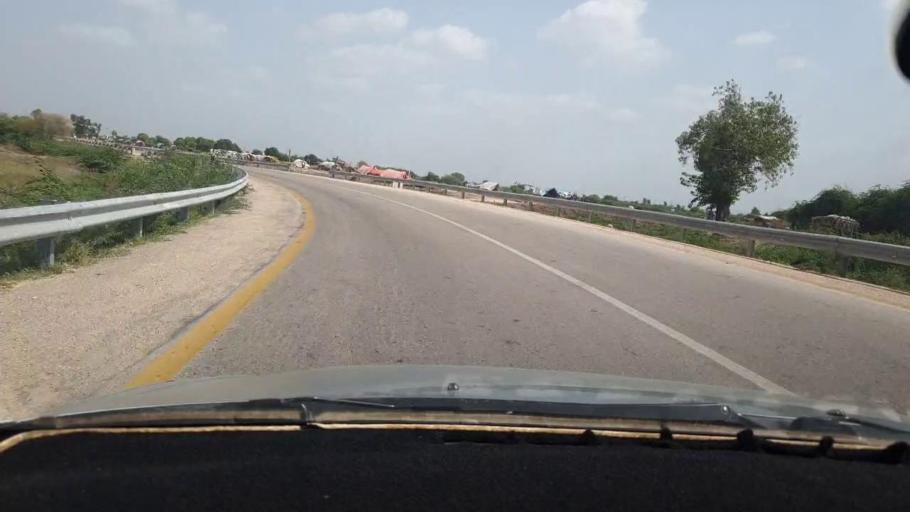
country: PK
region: Sindh
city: Digri
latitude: 25.1017
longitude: 69.1715
